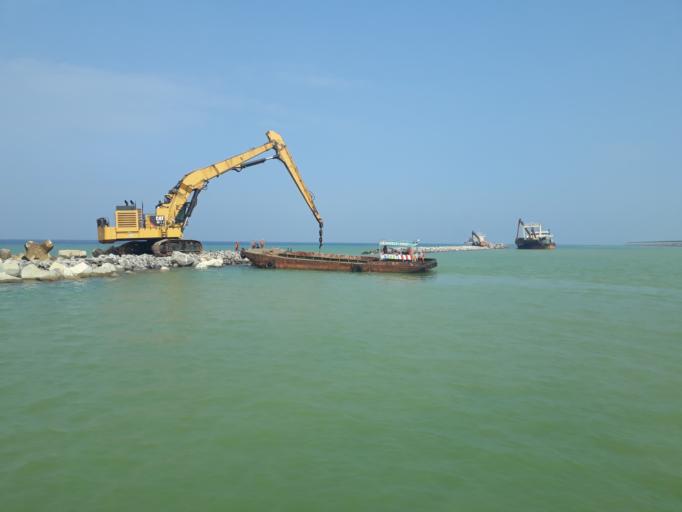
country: LK
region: Western
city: Colombo
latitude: 6.9322
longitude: 79.8209
